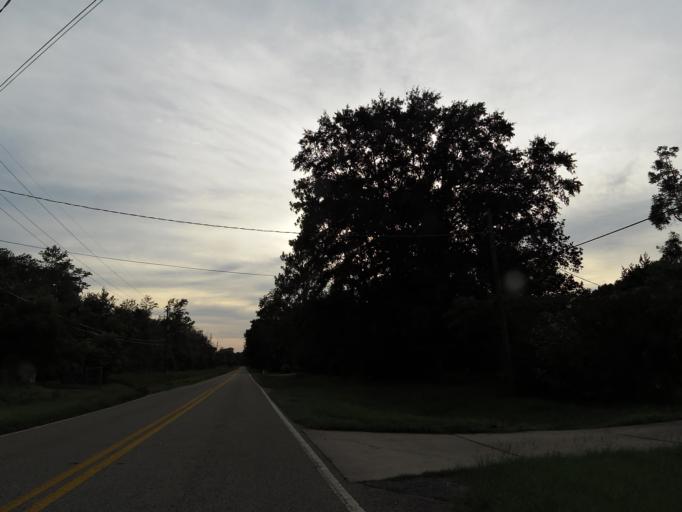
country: US
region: Florida
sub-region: Duval County
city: Jacksonville
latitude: 30.3943
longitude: -81.7453
